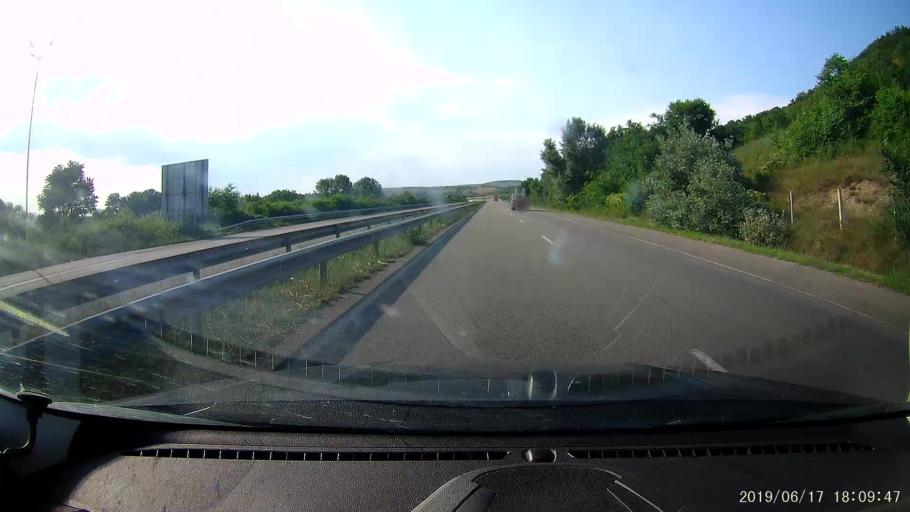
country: BG
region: Khaskovo
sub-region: Obshtina Lyubimets
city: Lyubimets
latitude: 41.8651
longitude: 26.0862
